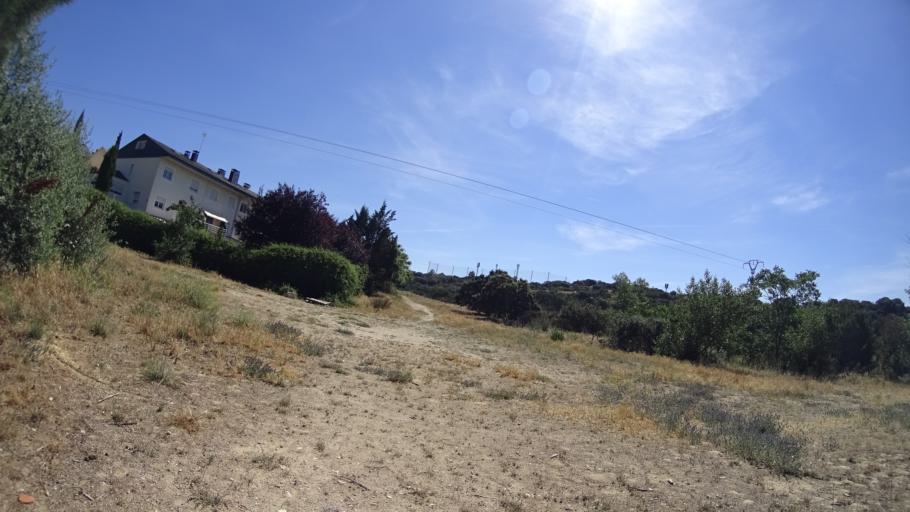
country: ES
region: Madrid
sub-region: Provincia de Madrid
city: Torrelodones
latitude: 40.5934
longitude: -3.9595
